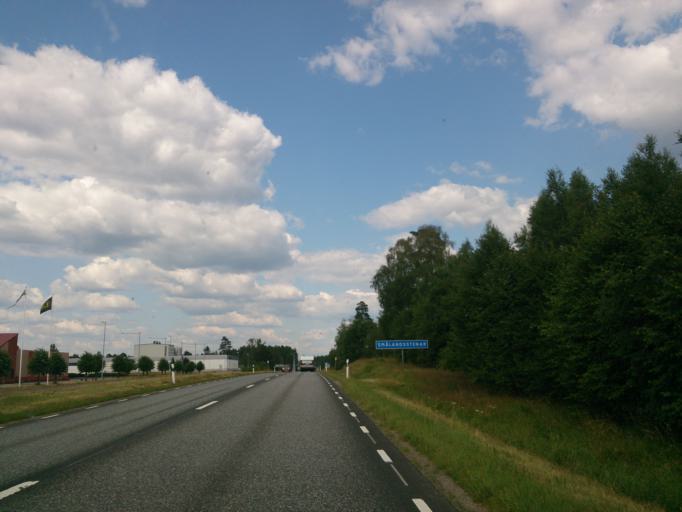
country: SE
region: Joenkoeping
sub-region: Gislaveds Kommun
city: Smalandsstenar
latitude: 57.1443
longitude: 13.3877
